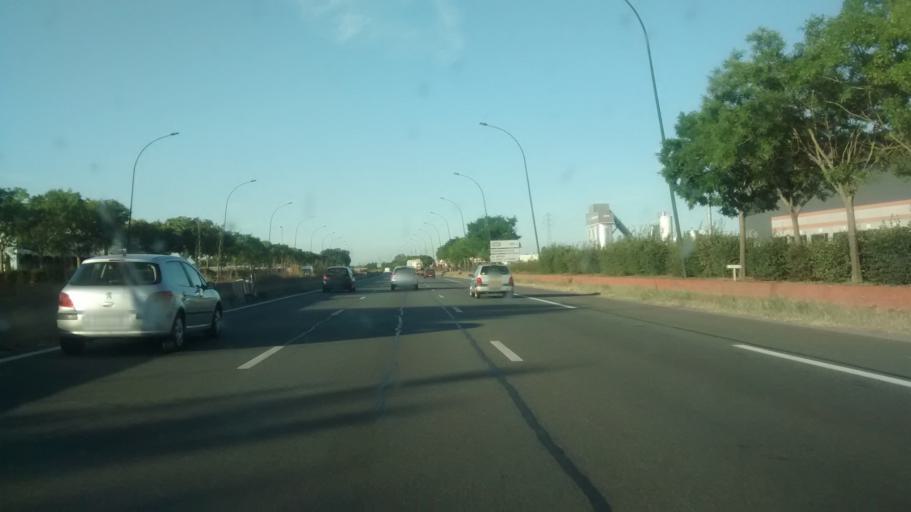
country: FR
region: Midi-Pyrenees
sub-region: Departement de la Haute-Garonne
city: Portet-sur-Garonne
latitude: 43.5447
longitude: 1.4008
